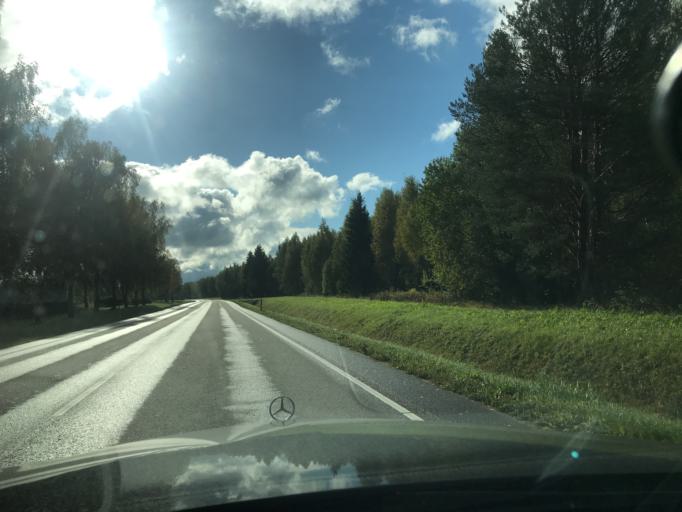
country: EE
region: Valgamaa
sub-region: Torva linn
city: Torva
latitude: 57.9873
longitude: 25.9417
